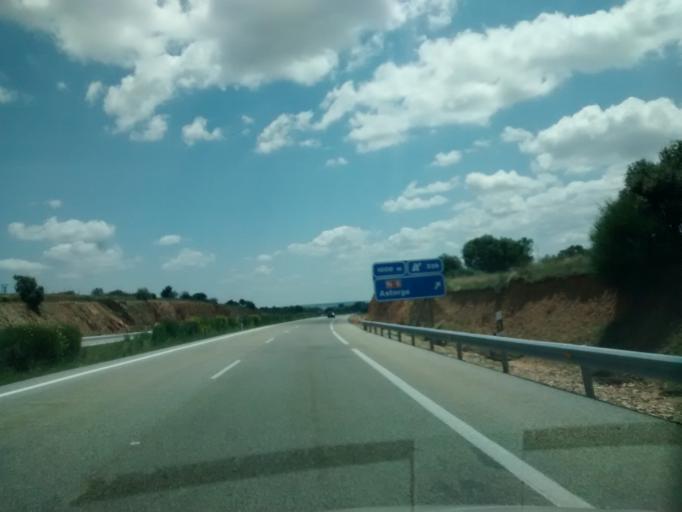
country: ES
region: Castille and Leon
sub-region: Provincia de Leon
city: Brazuelo
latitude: 42.4835
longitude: -6.1120
